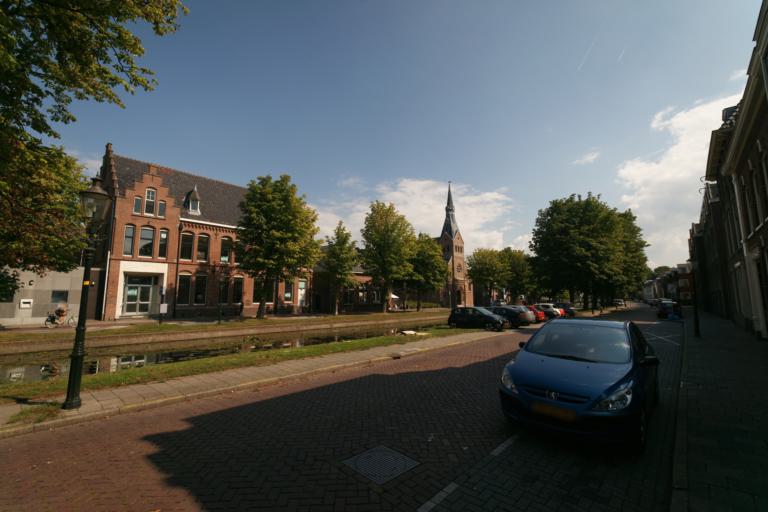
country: NL
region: North Holland
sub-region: Gemeente Weesp
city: Weesp
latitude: 52.3060
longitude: 5.0423
